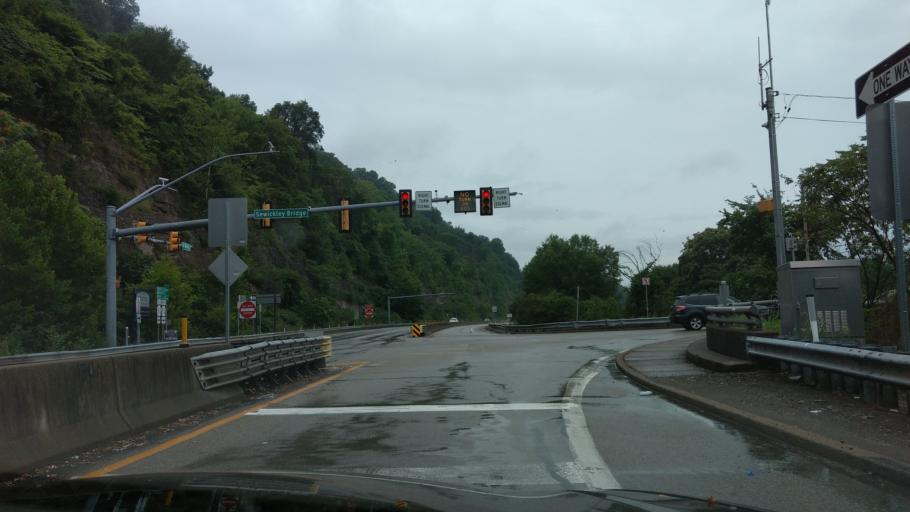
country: US
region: Pennsylvania
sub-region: Allegheny County
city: Sewickley
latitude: 40.5308
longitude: -80.1896
